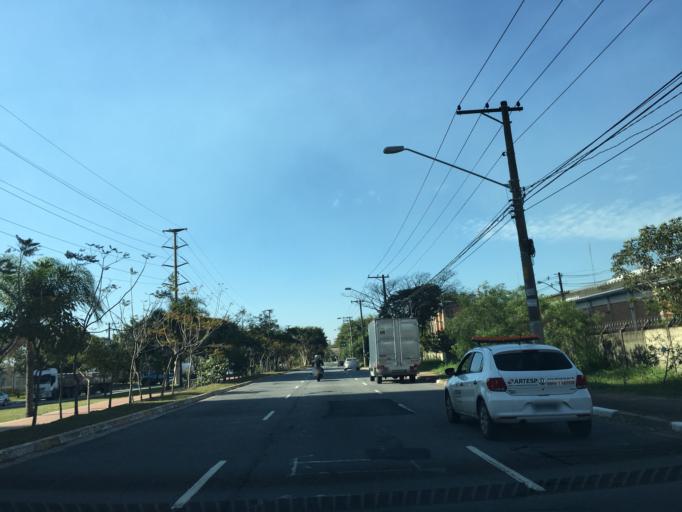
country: BR
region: Sao Paulo
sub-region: Osasco
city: Osasco
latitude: -23.5558
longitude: -46.7373
